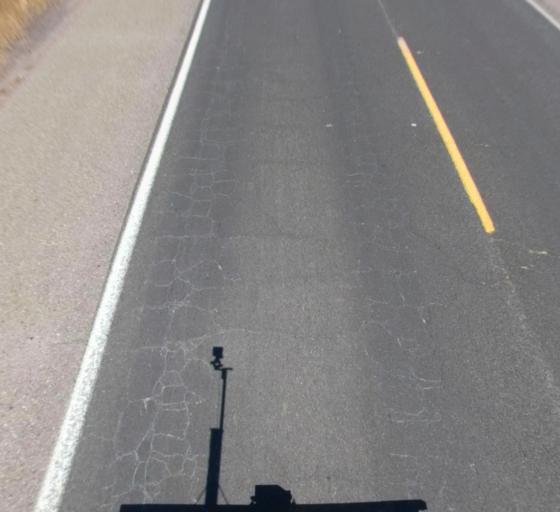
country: US
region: California
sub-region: Madera County
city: Parkwood
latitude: 36.9238
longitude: -120.0770
